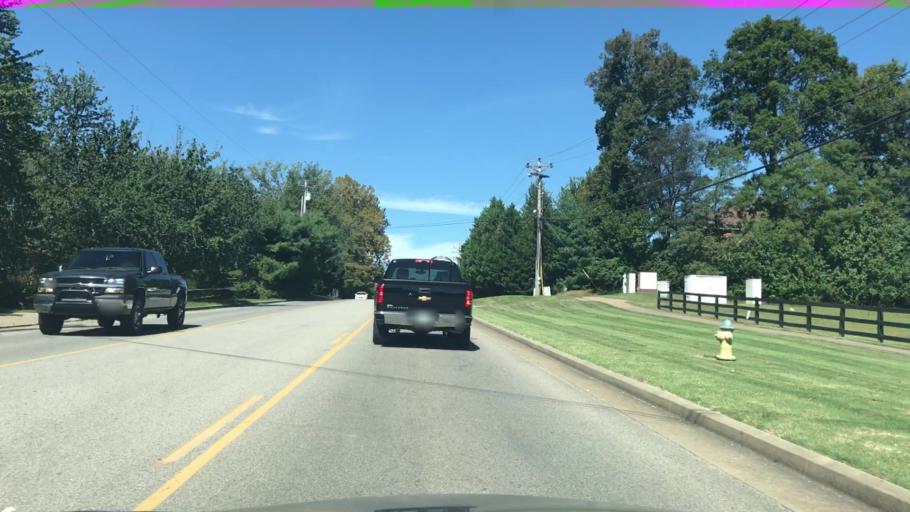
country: US
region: Tennessee
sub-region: Williamson County
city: Franklin
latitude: 35.9010
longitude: -86.8253
